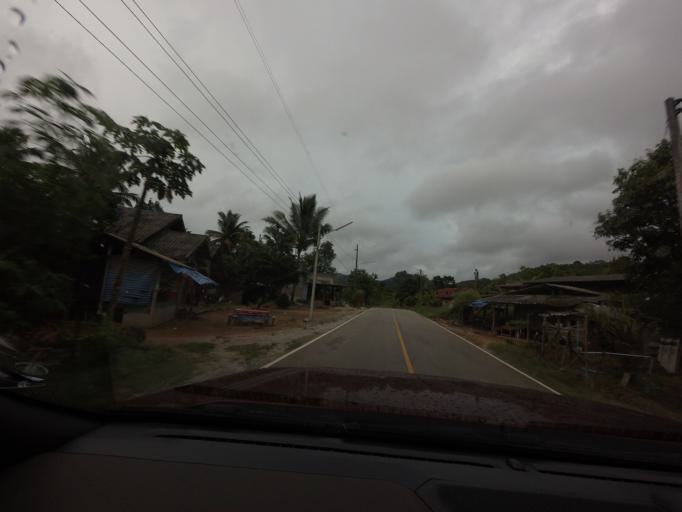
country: TH
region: Narathiwat
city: Chanae
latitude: 6.0357
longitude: 101.6918
